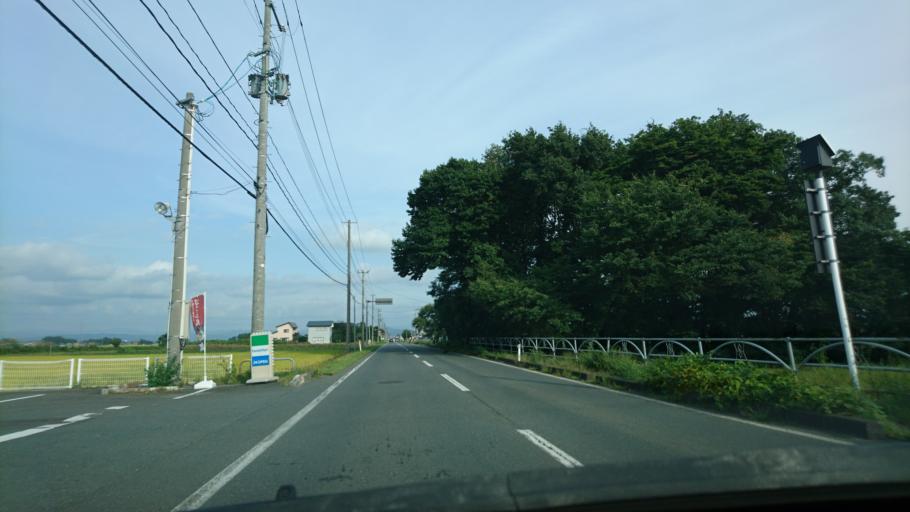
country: JP
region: Iwate
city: Kitakami
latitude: 39.3057
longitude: 141.0071
